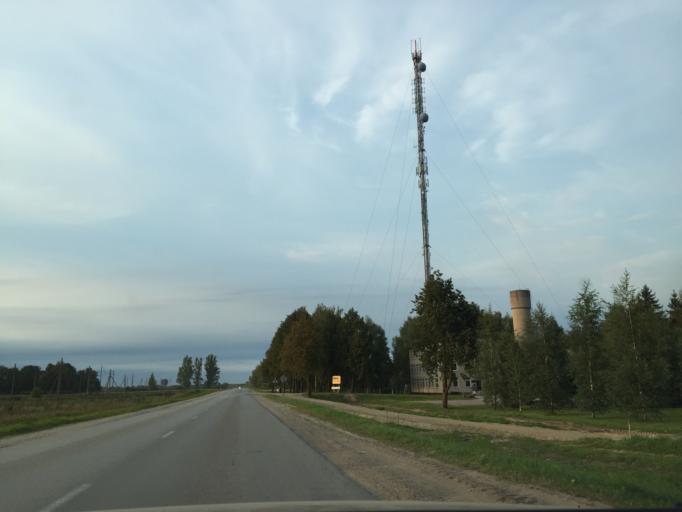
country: LT
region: Panevezys
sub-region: Birzai
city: Birzai
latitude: 56.2158
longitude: 24.7266
